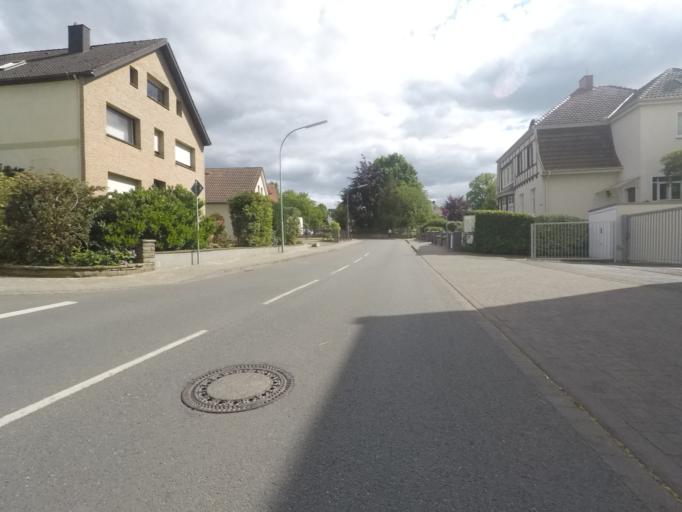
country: DE
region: North Rhine-Westphalia
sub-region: Regierungsbezirk Detmold
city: Herford
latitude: 52.1199
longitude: 8.6824
